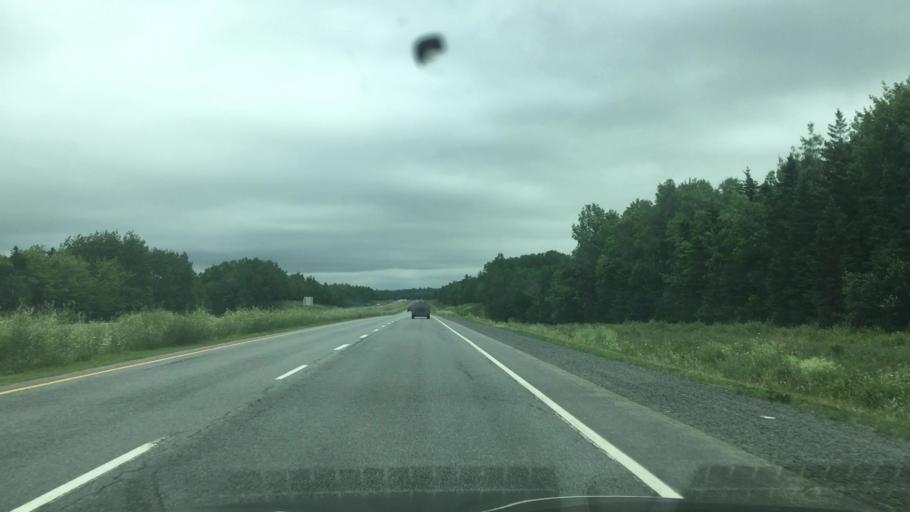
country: CA
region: Nova Scotia
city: Cole Harbour
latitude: 45.0059
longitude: -63.4825
